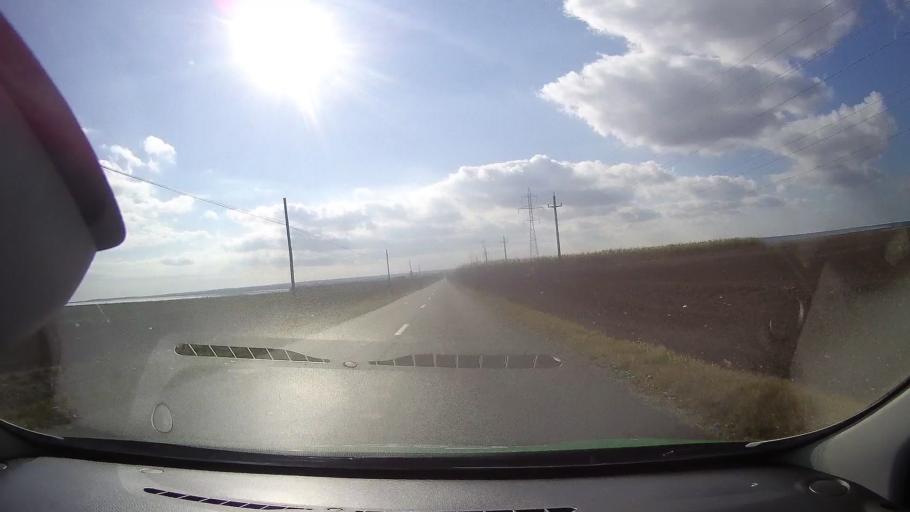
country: RO
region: Constanta
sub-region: Comuna Istria
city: Istria
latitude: 44.5536
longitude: 28.6969
